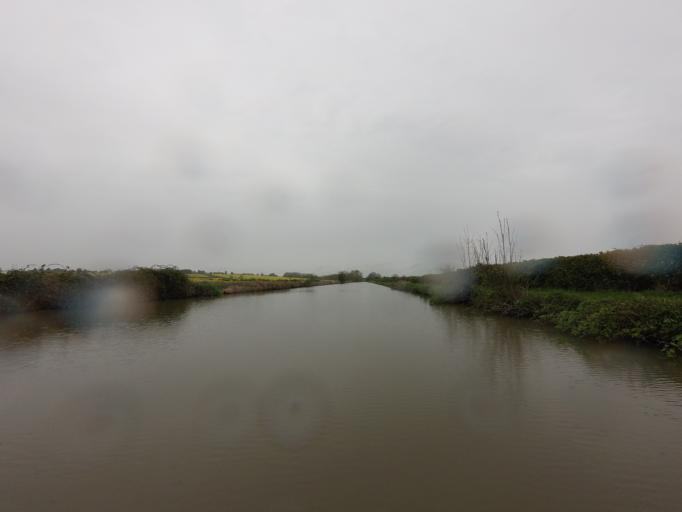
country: GB
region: England
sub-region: Northamptonshire
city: Hartwell
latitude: 52.1057
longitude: -0.8869
